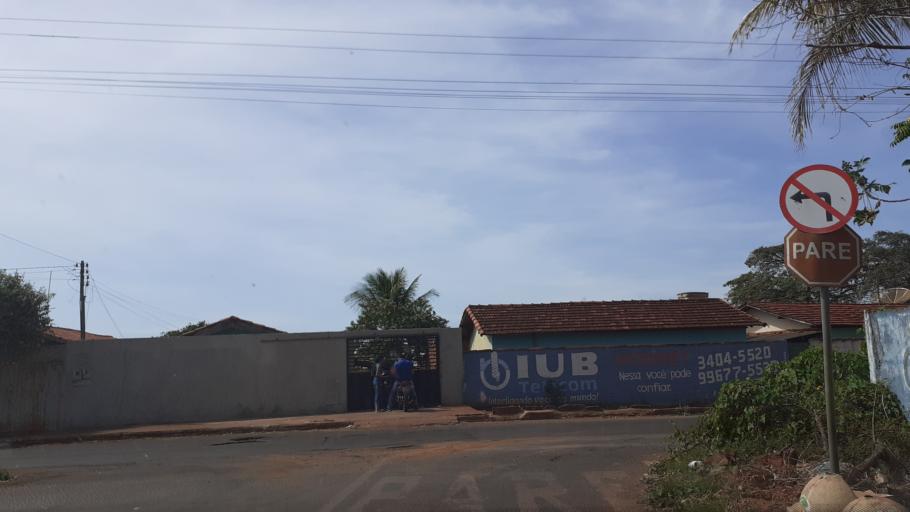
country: BR
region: Goias
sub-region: Itumbiara
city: Itumbiara
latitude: -18.4132
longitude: -49.2302
